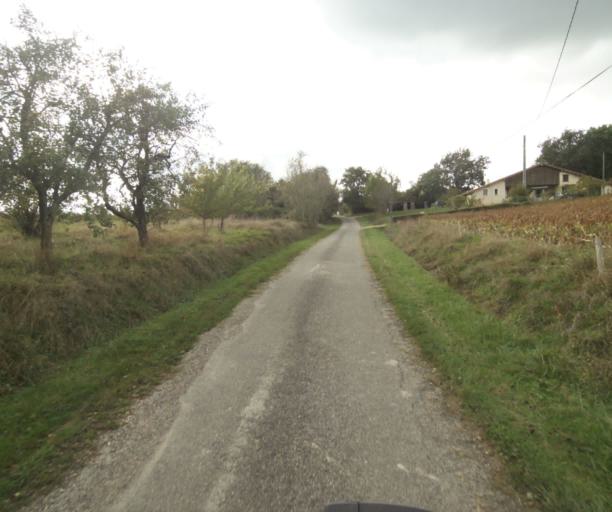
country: FR
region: Midi-Pyrenees
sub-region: Departement de la Haute-Garonne
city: Launac
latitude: 43.8258
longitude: 1.1023
